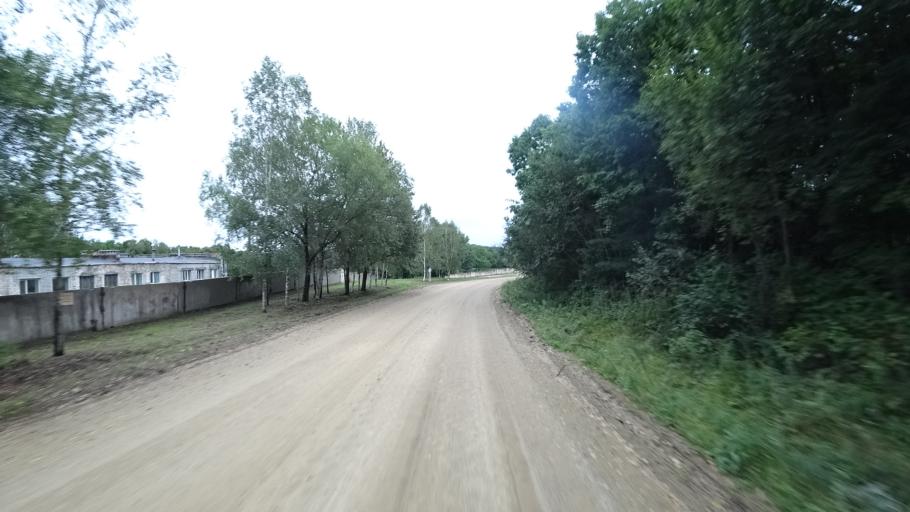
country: RU
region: Primorskiy
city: Rettikhovka
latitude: 44.1763
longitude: 132.8493
